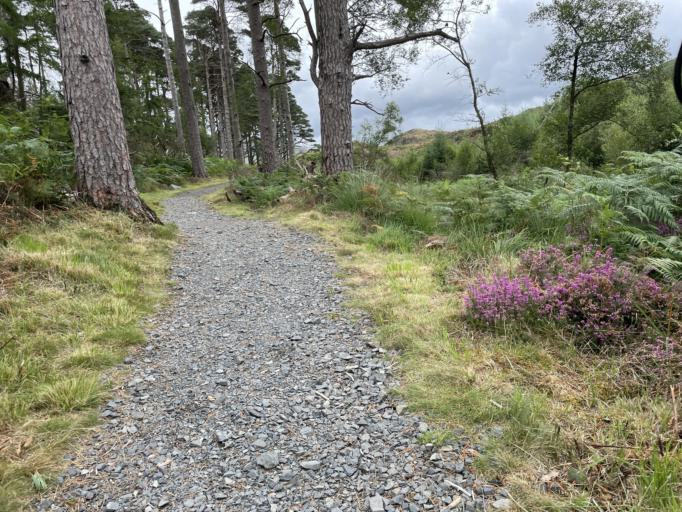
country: GB
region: Scotland
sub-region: Dumfries and Galloway
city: Newton Stewart
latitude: 55.0828
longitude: -4.4982
